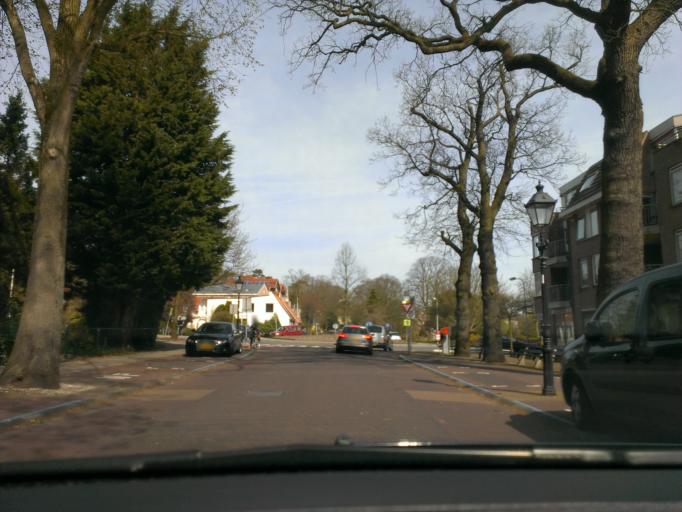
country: NL
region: North Holland
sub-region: Gemeente Bloemendaal
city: Bloemendaal
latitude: 52.3916
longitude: 4.6095
